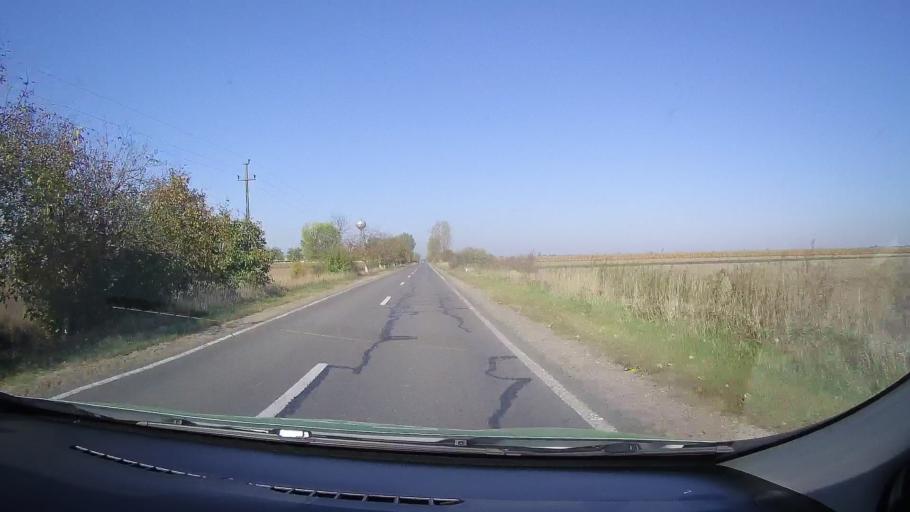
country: RO
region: Satu Mare
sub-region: Comuna Urziceni
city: Urziceni
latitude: 47.7198
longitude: 22.4172
